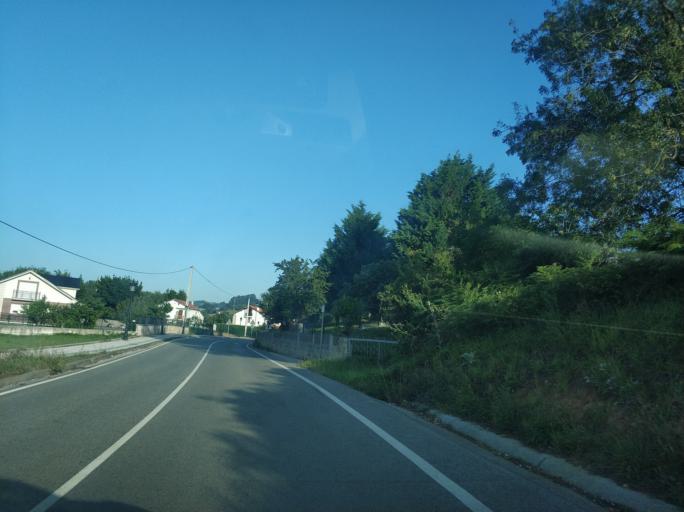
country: ES
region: Cantabria
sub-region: Provincia de Cantabria
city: Santa Cruz de Bezana
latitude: 43.4027
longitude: -3.9436
